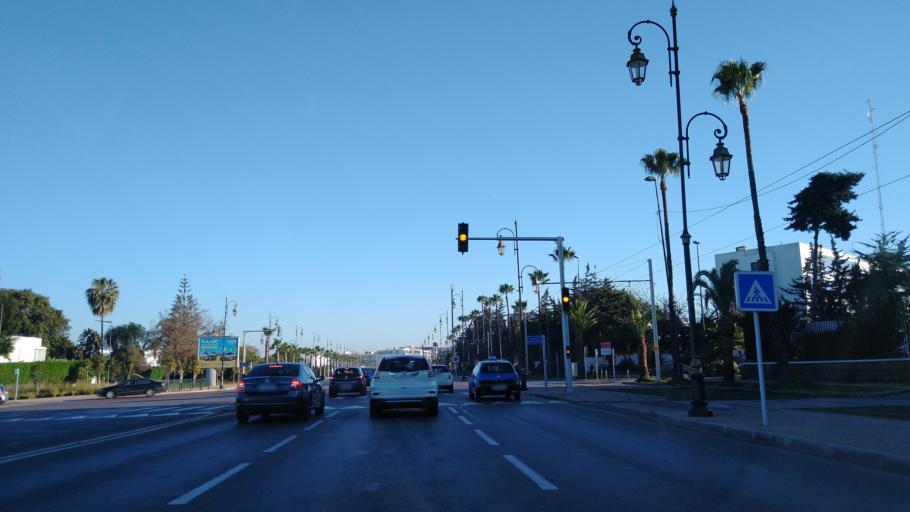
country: MA
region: Rabat-Sale-Zemmour-Zaer
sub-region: Rabat
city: Rabat
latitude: 33.9930
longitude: -6.8544
